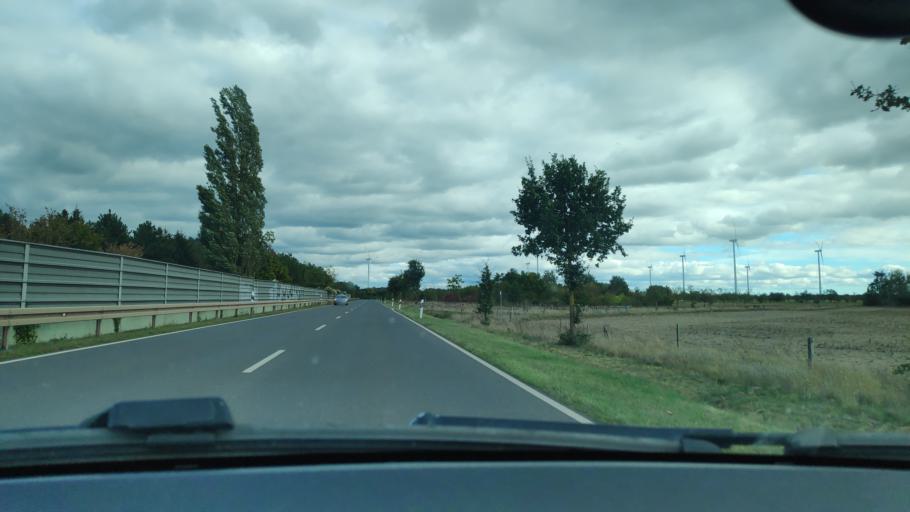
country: DE
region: Saxony-Anhalt
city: Schermen
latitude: 52.2222
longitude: 11.8083
